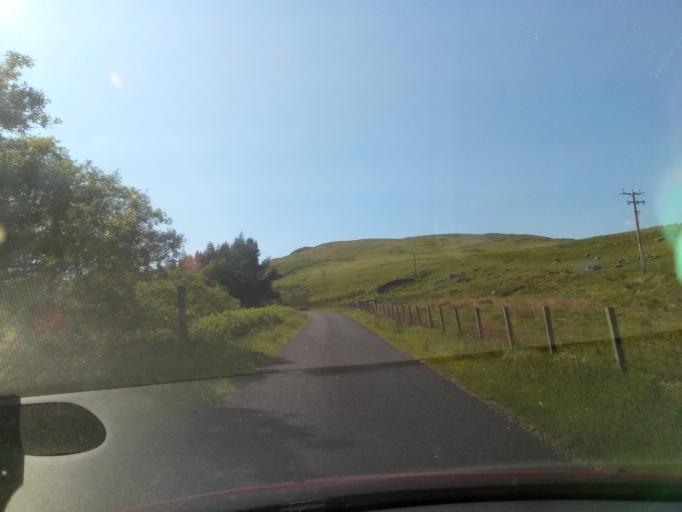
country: GB
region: Scotland
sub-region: The Scottish Borders
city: Peebles
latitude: 55.4957
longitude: -3.2400
